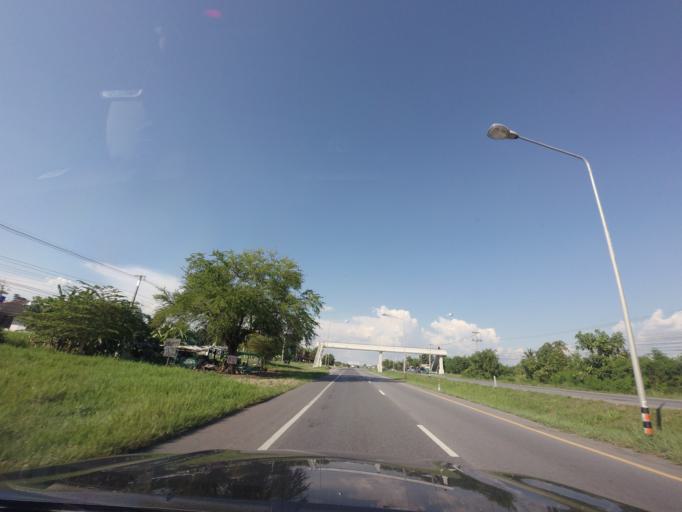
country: TH
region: Khon Kaen
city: Non Sila
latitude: 15.9508
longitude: 102.6831
